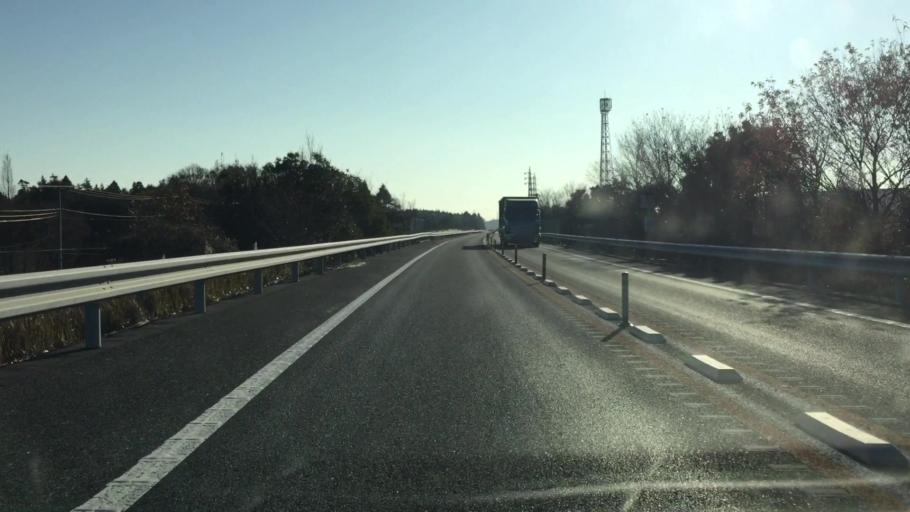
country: JP
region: Ibaraki
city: Ami
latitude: 35.9935
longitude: 140.2144
